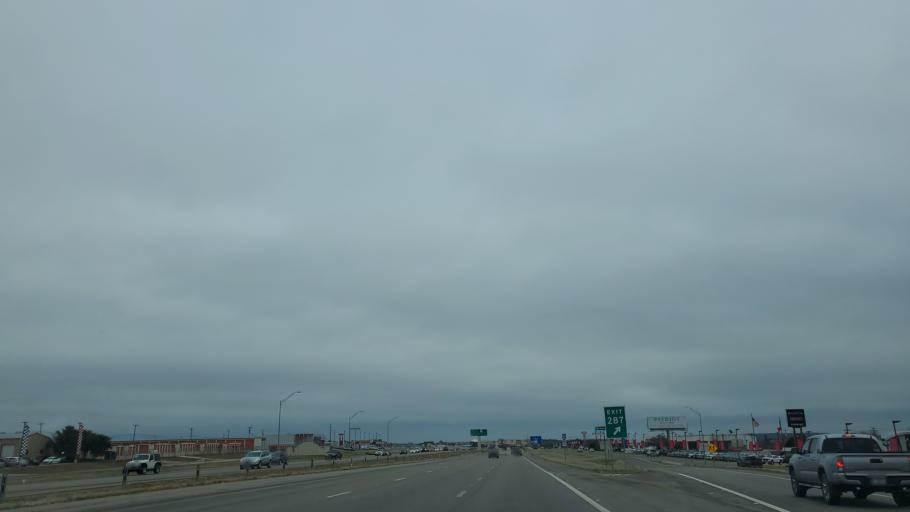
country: US
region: Texas
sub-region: Bell County
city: Harker Heights
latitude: 31.0794
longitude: -97.6969
